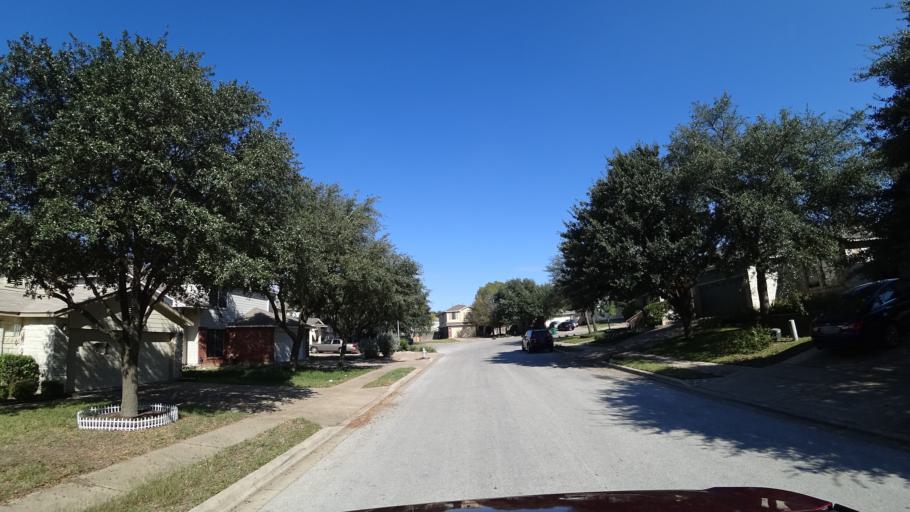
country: US
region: Texas
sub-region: Travis County
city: Windemere
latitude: 30.4424
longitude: -97.6583
